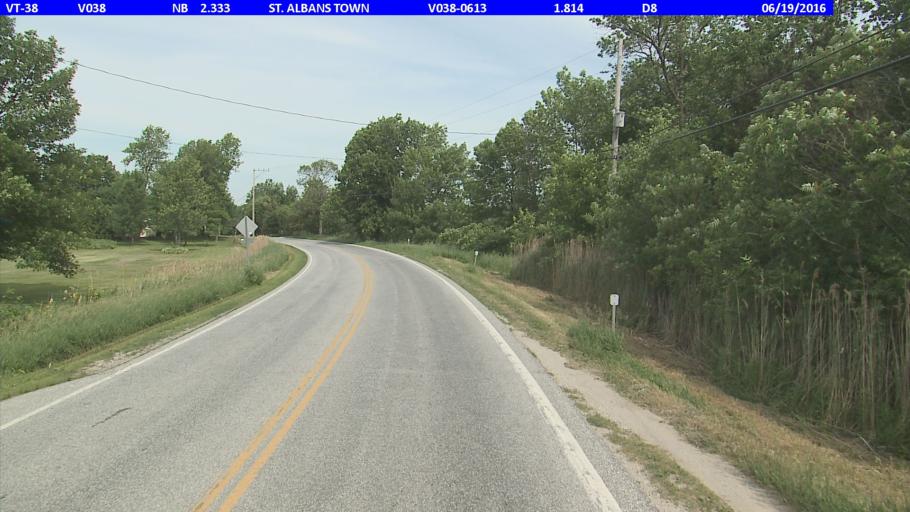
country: US
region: Vermont
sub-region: Franklin County
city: Saint Albans
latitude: 44.8454
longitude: -73.1098
